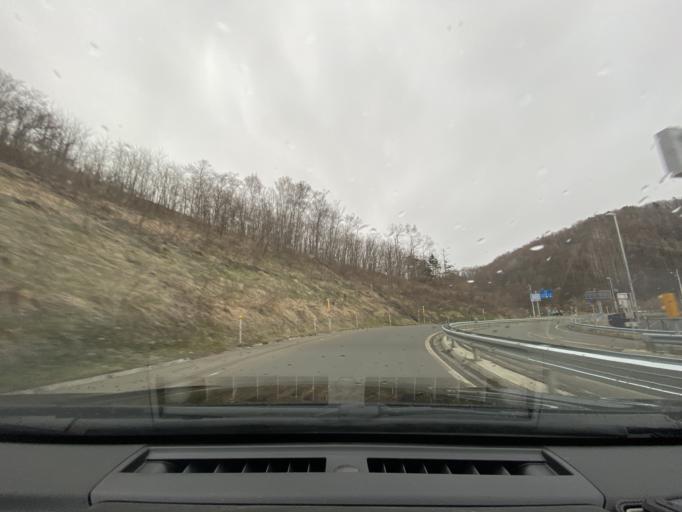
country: JP
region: Hokkaido
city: Kitami
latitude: 43.7946
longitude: 143.9161
